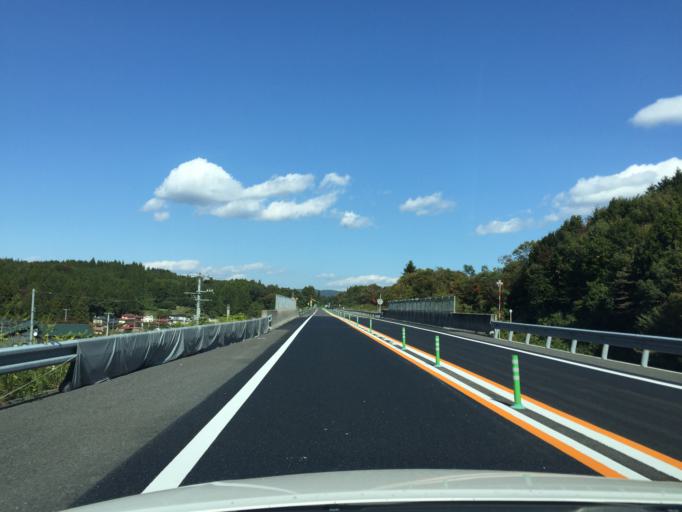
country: JP
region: Fukushima
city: Funehikimachi-funehiki
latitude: 37.2828
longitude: 140.6016
